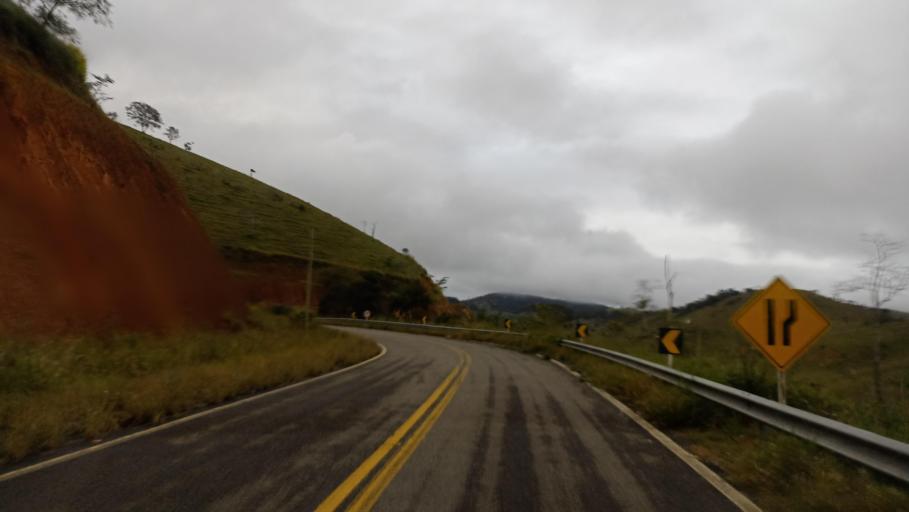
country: BR
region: Minas Gerais
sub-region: Joaima
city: Joaima
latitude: -16.6874
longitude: -40.5222
